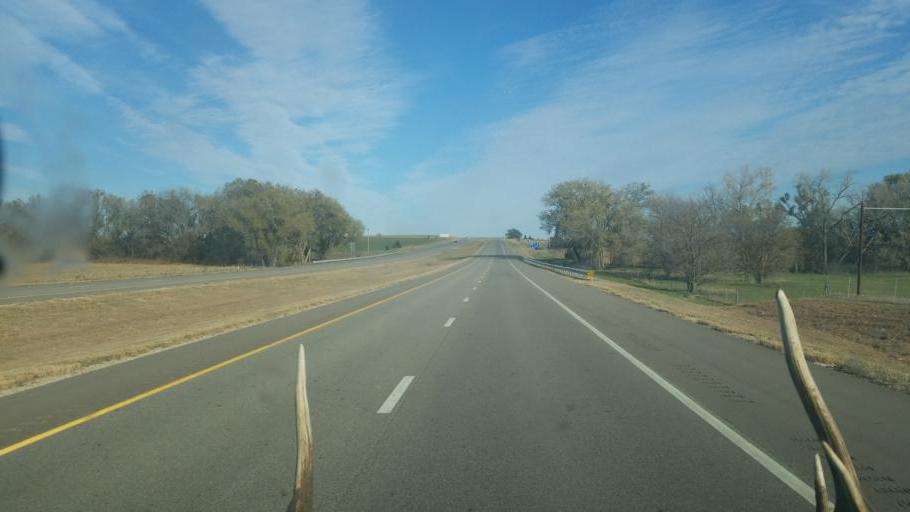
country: US
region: Kansas
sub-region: Russell County
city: Russell
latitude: 38.8565
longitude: -98.5984
